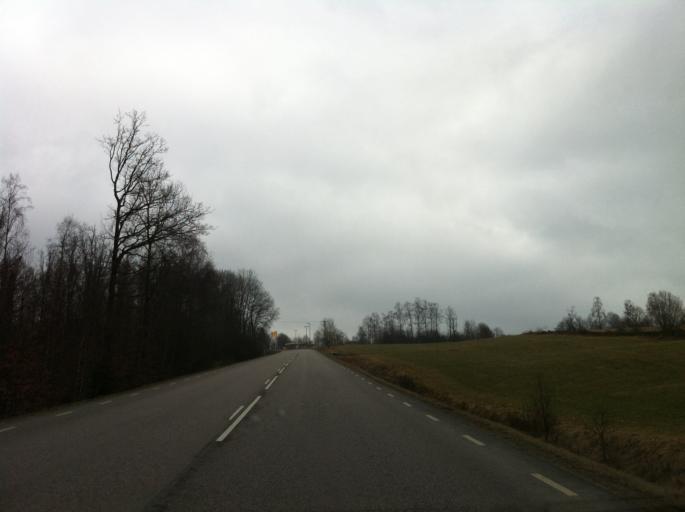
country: SE
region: Vaestra Goetaland
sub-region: Boras Kommun
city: Dalsjofors
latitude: 57.7730
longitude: 13.1034
